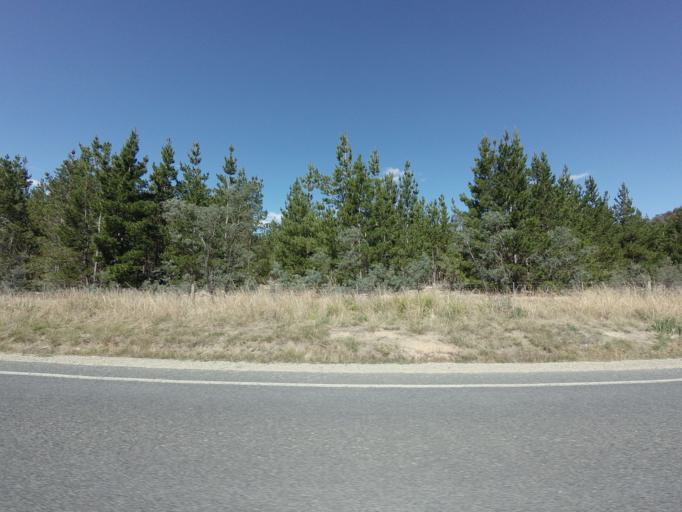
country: AU
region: Tasmania
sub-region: Break O'Day
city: St Helens
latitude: -41.6811
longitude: 147.8890
